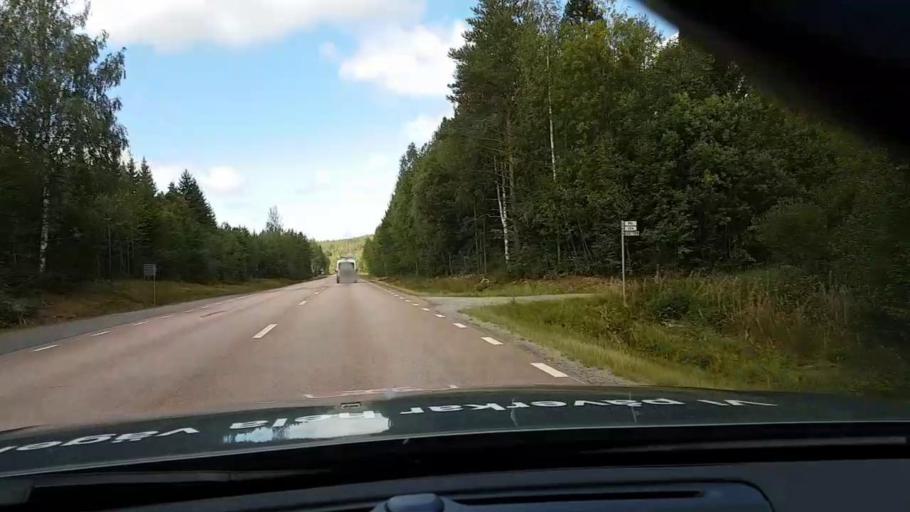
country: SE
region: Vaesternorrland
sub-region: OErnskoeldsviks Kommun
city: Bjasta
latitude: 63.3753
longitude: 18.4292
